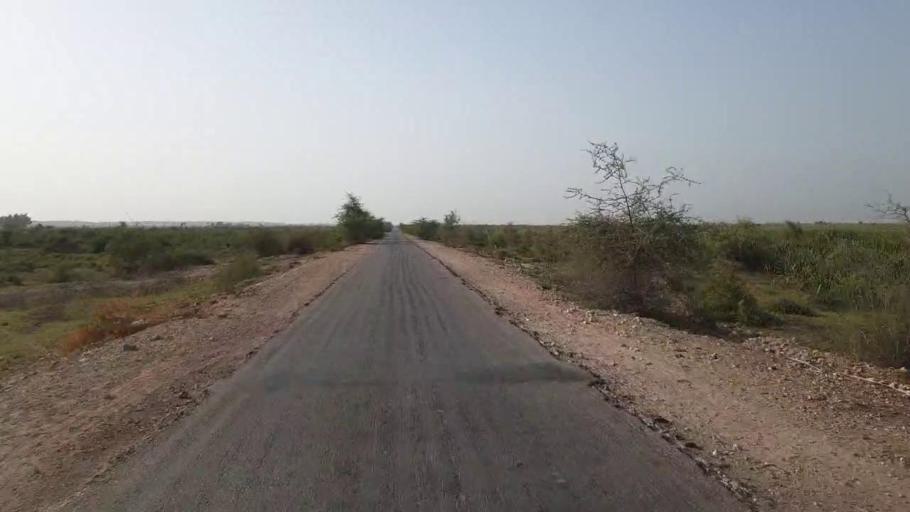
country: PK
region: Sindh
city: Jam Sahib
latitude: 26.4415
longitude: 68.8662
